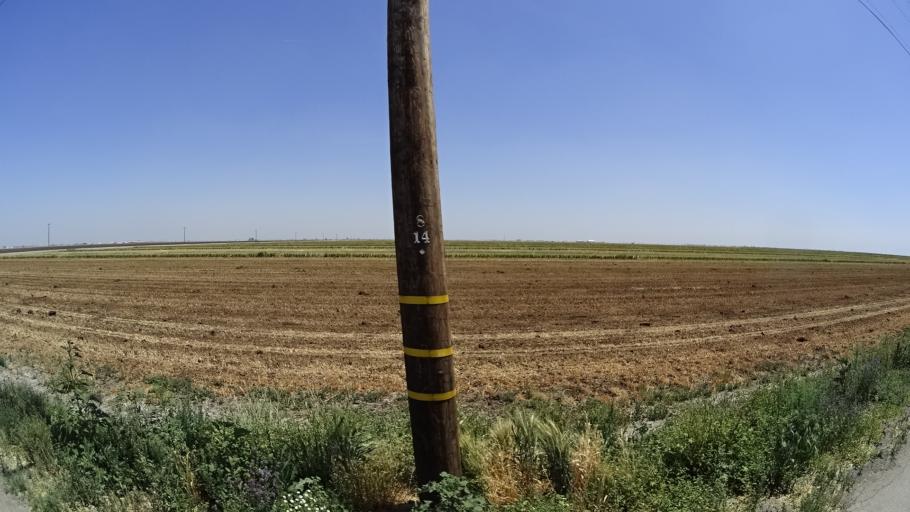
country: US
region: California
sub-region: Kings County
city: Corcoran
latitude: 36.1659
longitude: -119.6459
